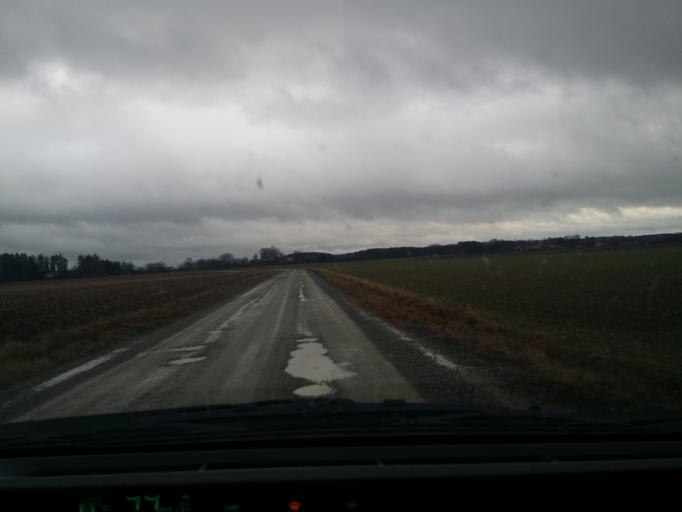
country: SE
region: Vaestmanland
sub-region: Vasteras
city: Skultuna
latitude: 59.7827
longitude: 16.4487
